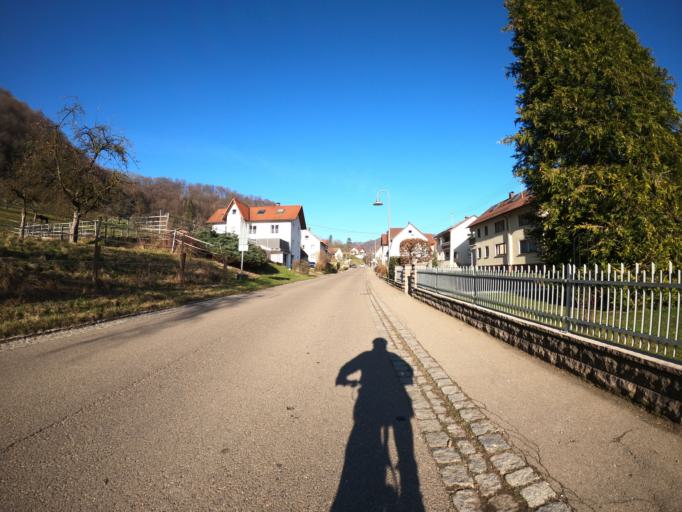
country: DE
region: Baden-Wuerttemberg
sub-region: Regierungsbezirk Stuttgart
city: Bad Ditzenbach
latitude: 48.6117
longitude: 9.6785
